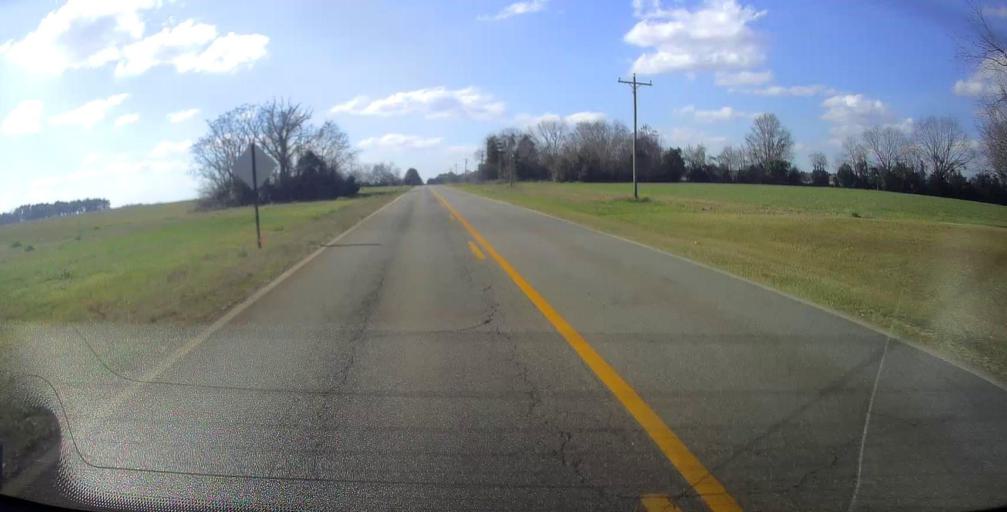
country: US
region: Georgia
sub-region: Laurens County
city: Dublin
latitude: 32.5633
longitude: -83.0182
